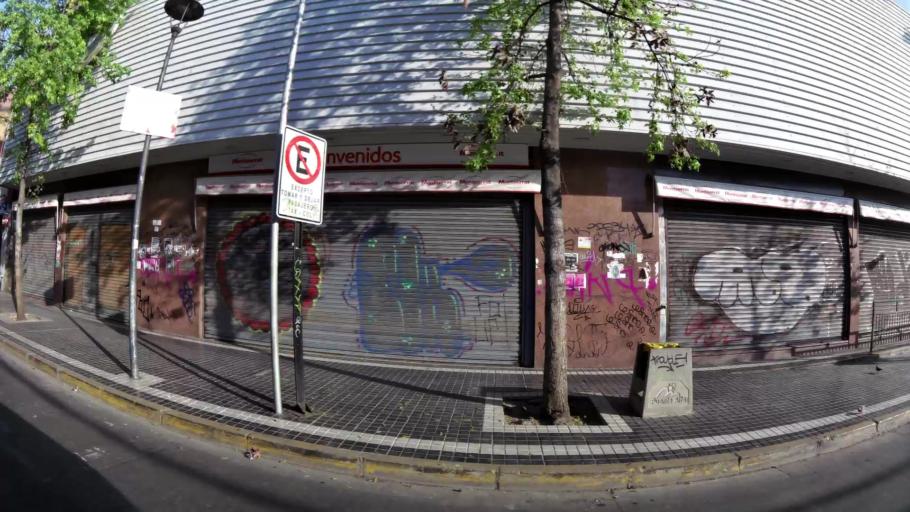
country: CL
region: Santiago Metropolitan
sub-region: Provincia de Cordillera
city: Puente Alto
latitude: -33.6094
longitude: -70.5765
